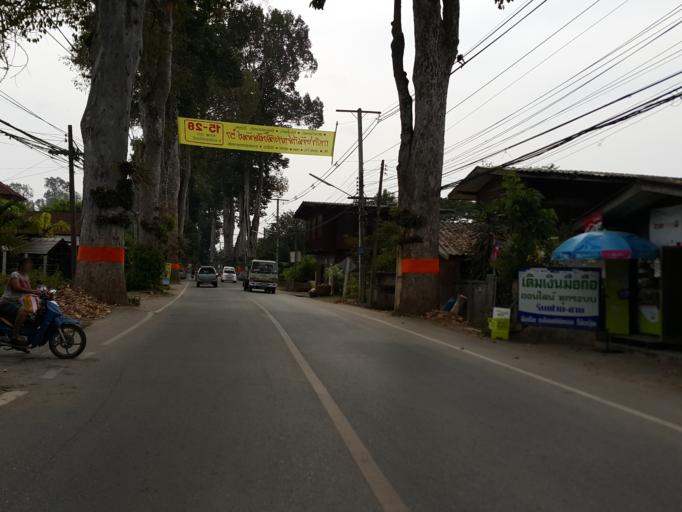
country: TH
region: Chiang Mai
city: Saraphi
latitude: 18.7084
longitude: 99.0405
